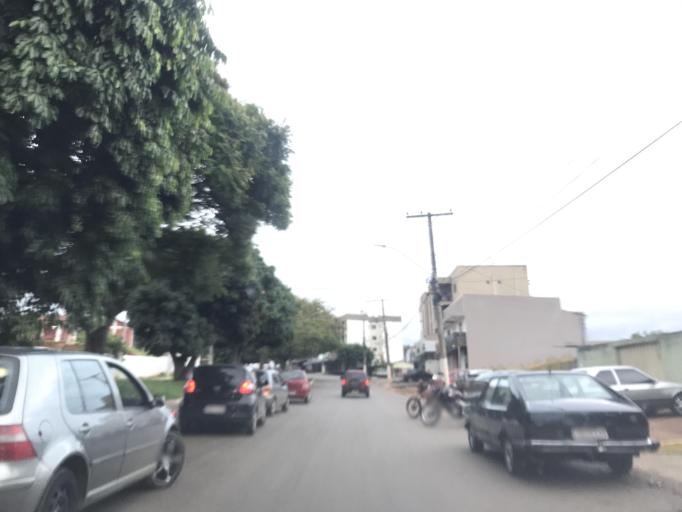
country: BR
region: Goias
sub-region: Luziania
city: Luziania
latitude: -16.2600
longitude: -47.9580
